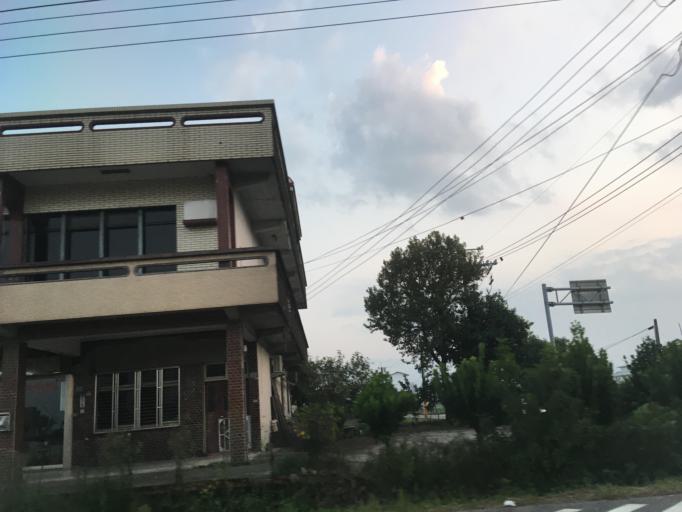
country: TW
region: Taiwan
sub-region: Yilan
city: Yilan
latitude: 24.6927
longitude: 121.7807
